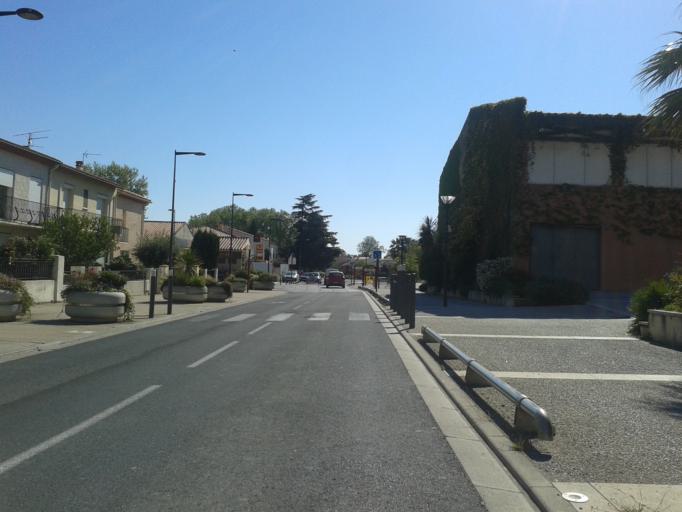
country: FR
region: Languedoc-Roussillon
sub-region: Departement des Pyrenees-Orientales
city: Toulouges
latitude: 42.6726
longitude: 2.8308
